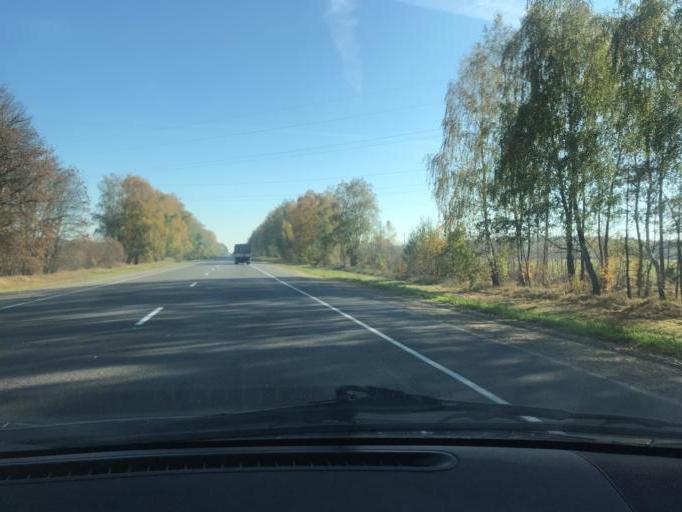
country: BY
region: Brest
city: Ivanava
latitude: 52.1546
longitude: 25.5776
